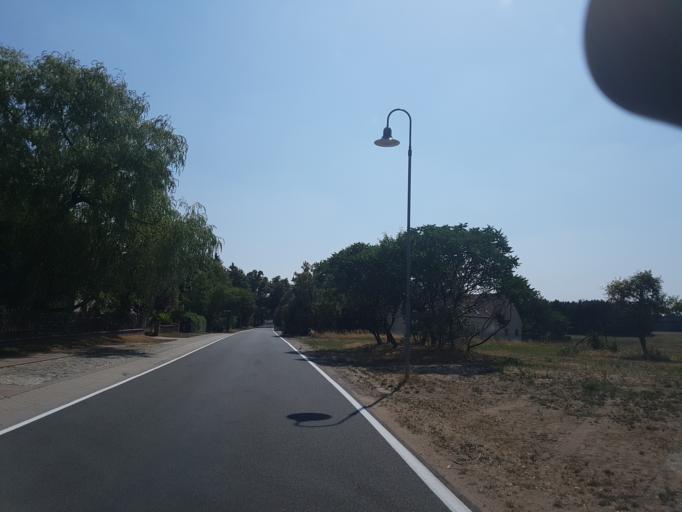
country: DE
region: Brandenburg
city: Wiesenburg
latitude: 52.0566
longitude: 12.3812
